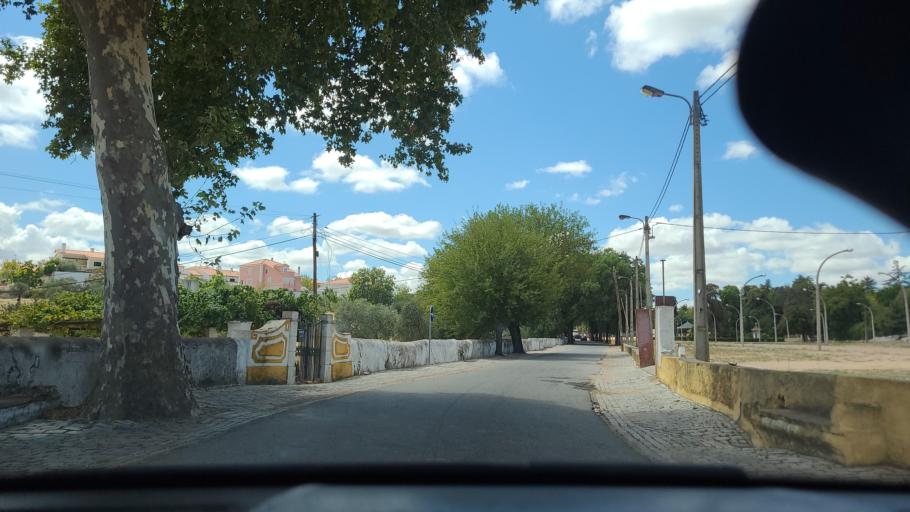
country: PT
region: Portalegre
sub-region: Elvas
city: Elvas
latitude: 38.8738
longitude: -7.1763
